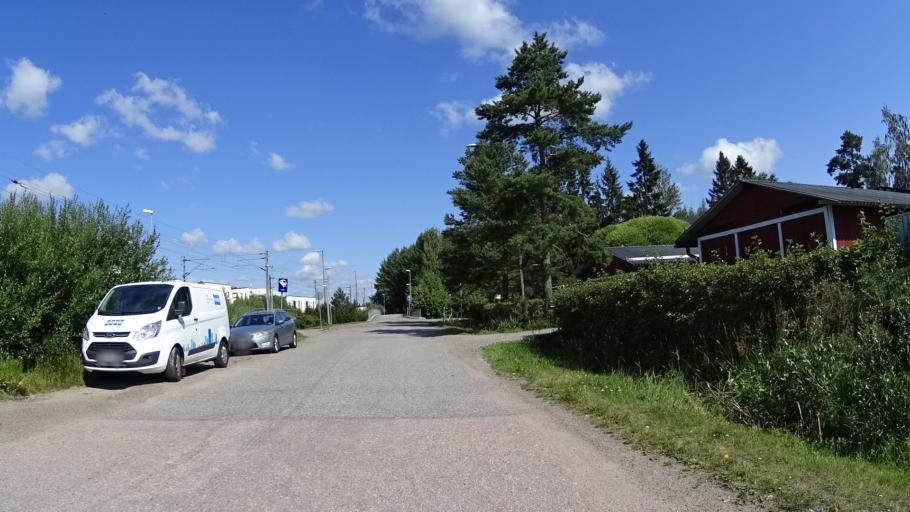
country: FI
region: Uusimaa
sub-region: Helsinki
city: Jaervenpaeae
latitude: 60.4589
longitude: 25.1015
